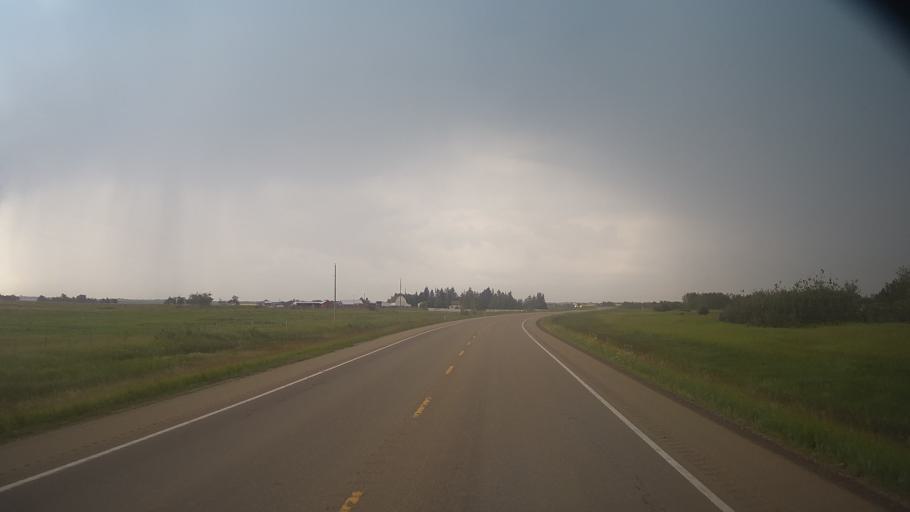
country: CA
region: Alberta
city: Tofield
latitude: 53.3288
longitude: -112.5719
